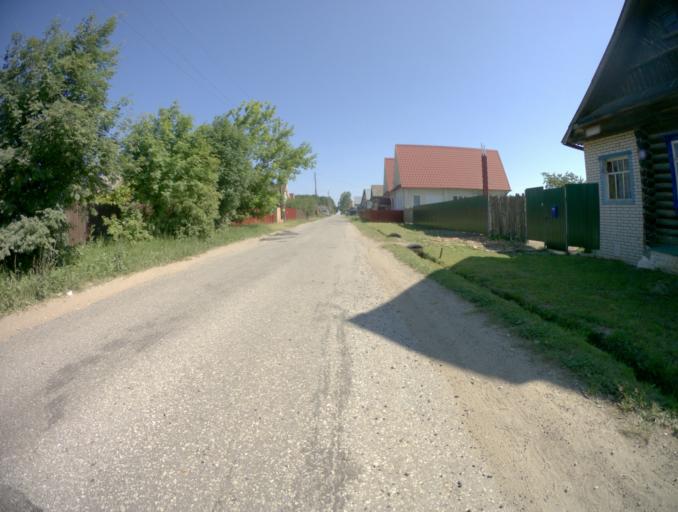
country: RU
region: Vladimir
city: Vyazniki
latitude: 56.2340
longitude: 42.1954
